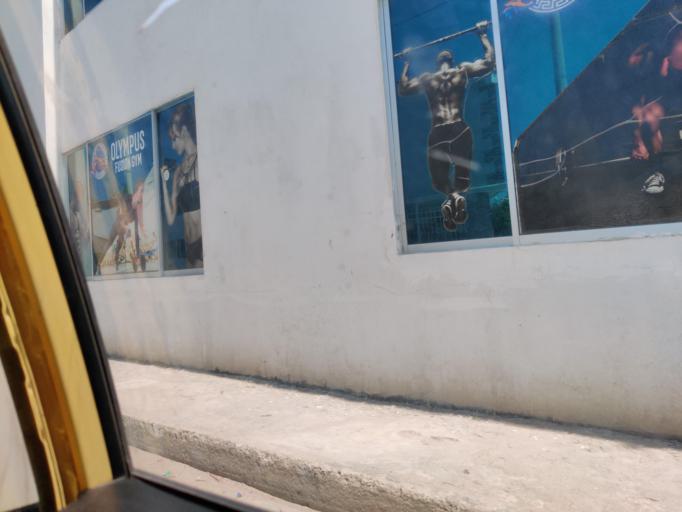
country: CO
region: Atlantico
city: Soledad
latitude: 10.9145
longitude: -74.8132
